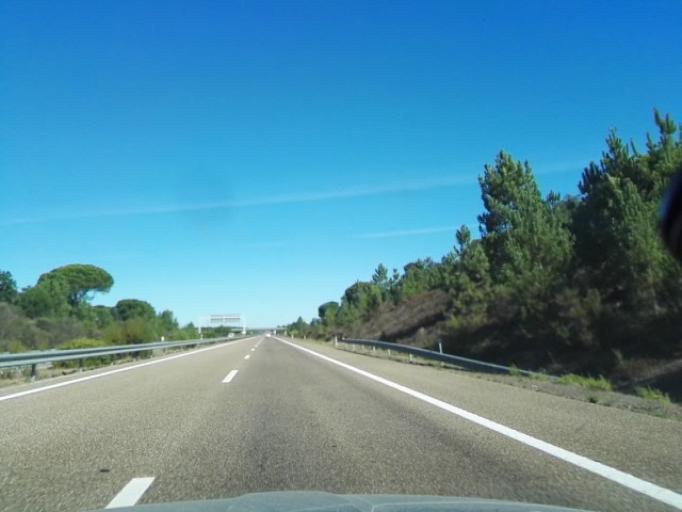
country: PT
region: Evora
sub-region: Vendas Novas
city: Vendas Novas
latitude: 38.6150
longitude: -8.6514
